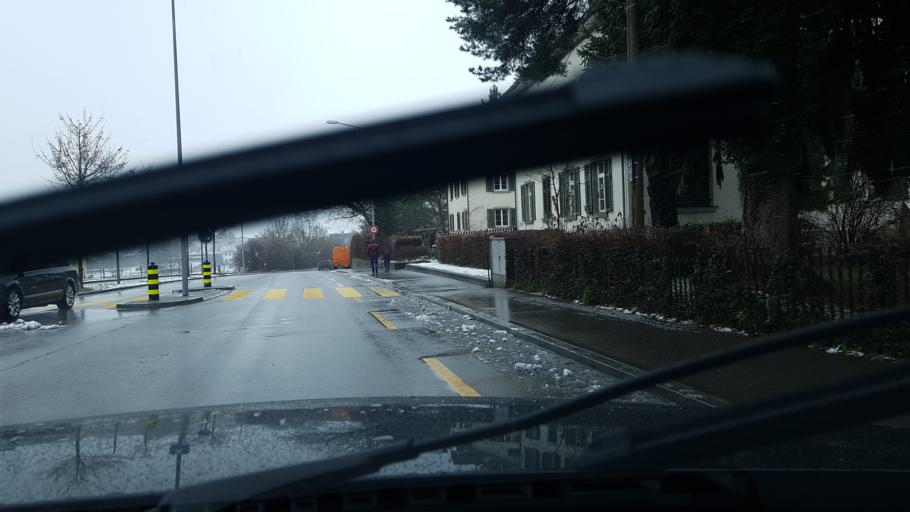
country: CH
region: Zurich
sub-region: Bezirk Zuerich
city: Zuerich (Kreis 11) / Affoltern
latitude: 47.4226
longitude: 8.5080
